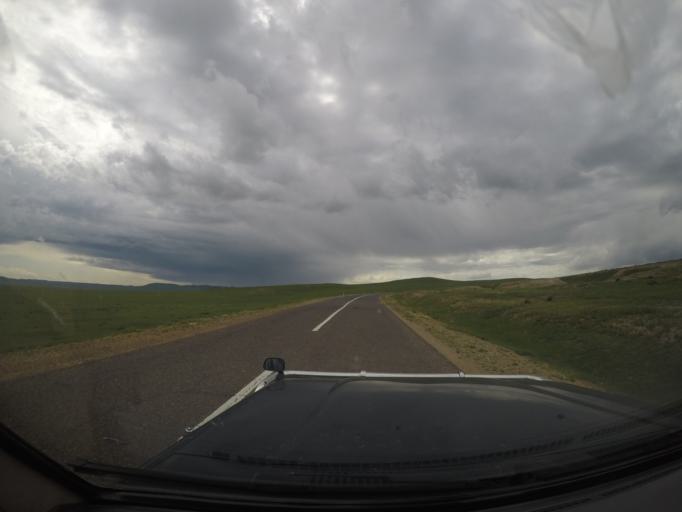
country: MN
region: Hentiy
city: Avraga
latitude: 47.4619
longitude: 109.5494
